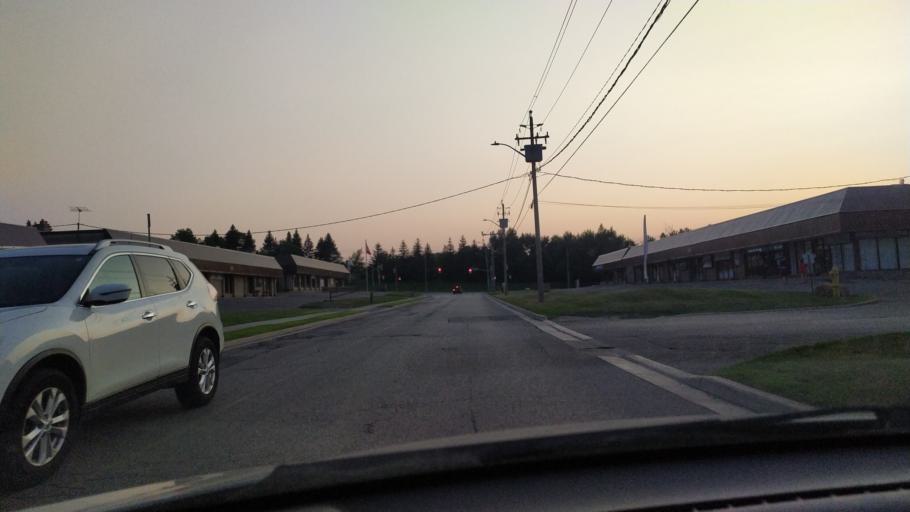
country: CA
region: Ontario
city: Kitchener
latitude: 43.4452
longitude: -80.5207
